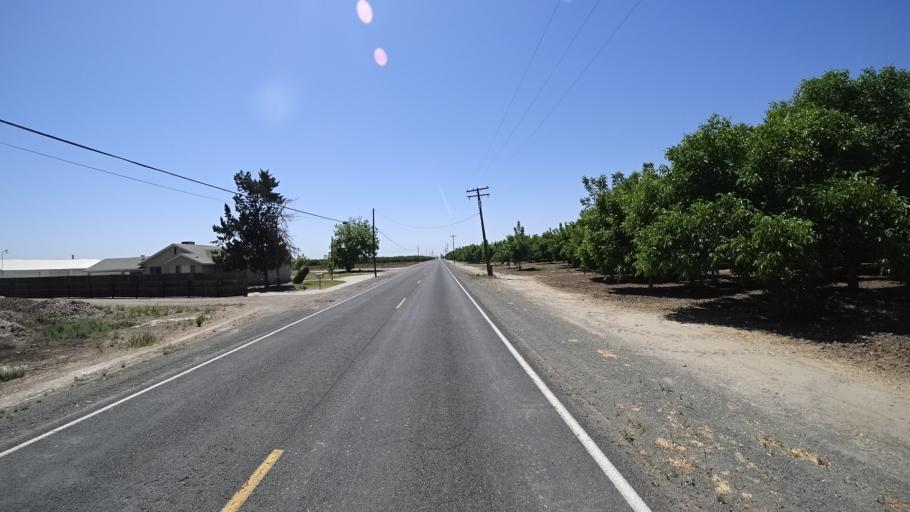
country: US
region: California
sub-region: Kings County
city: Armona
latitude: 36.2455
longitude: -119.7089
